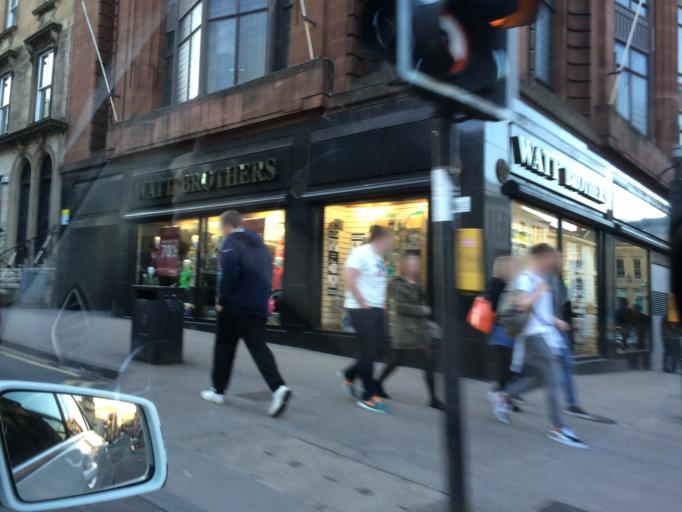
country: GB
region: Scotland
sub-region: Glasgow City
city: Glasgow
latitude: 55.8640
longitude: -4.2575
